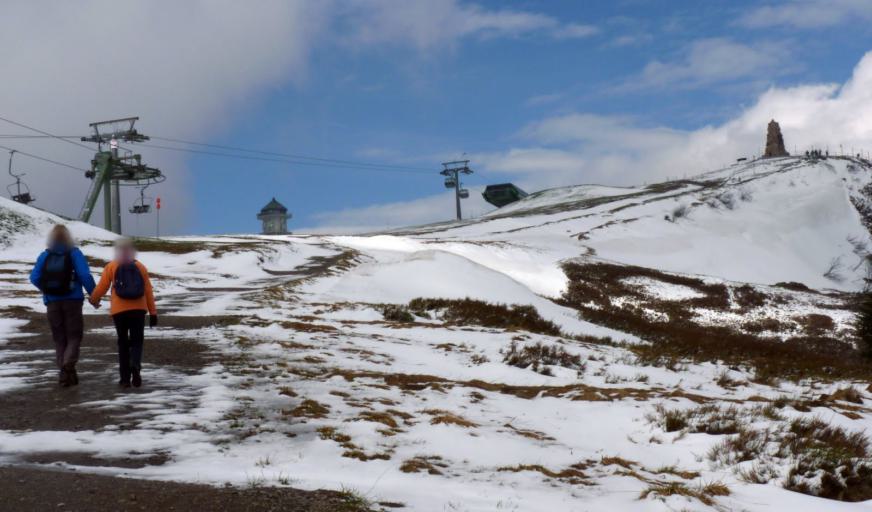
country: DE
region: Baden-Wuerttemberg
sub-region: Freiburg Region
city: Bernau
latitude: 47.8650
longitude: 8.0289
